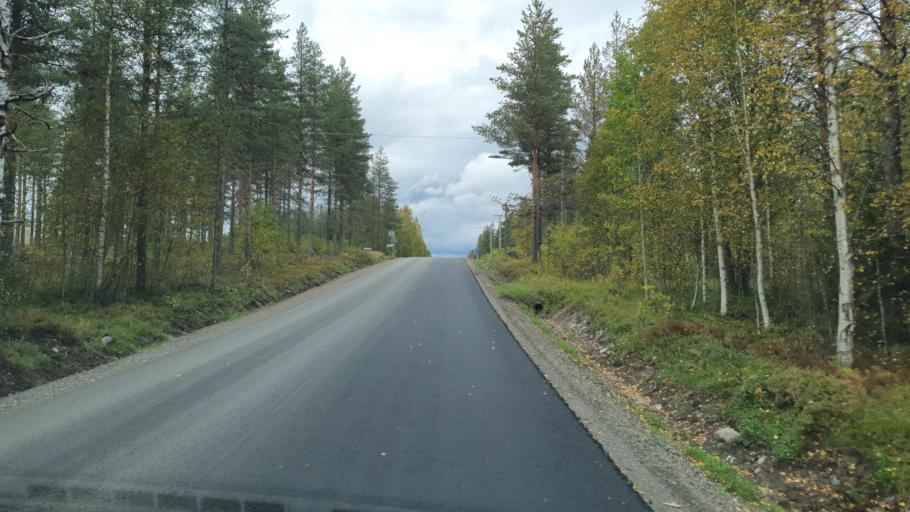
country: FI
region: Lapland
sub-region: Rovaniemi
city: Rovaniemi
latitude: 66.4258
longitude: 25.3979
